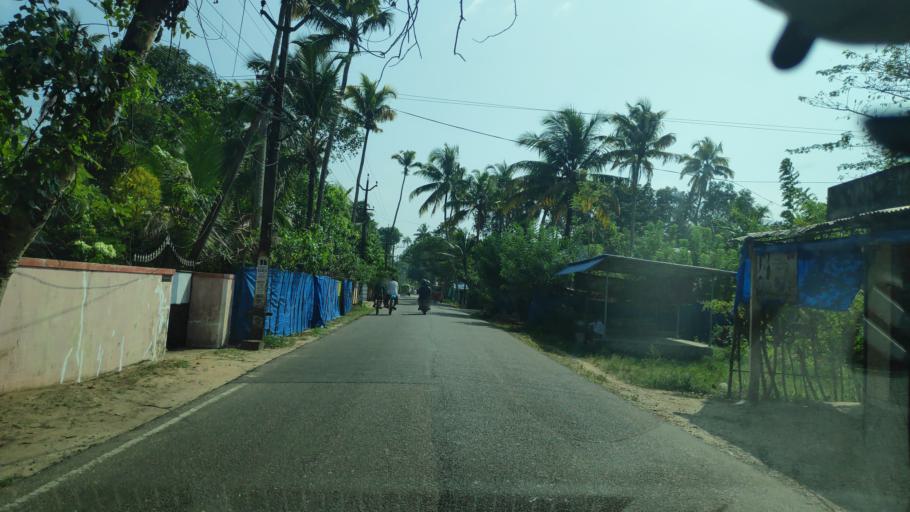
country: IN
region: Kerala
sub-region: Alappuzha
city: Vayalar
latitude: 9.6514
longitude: 76.2997
